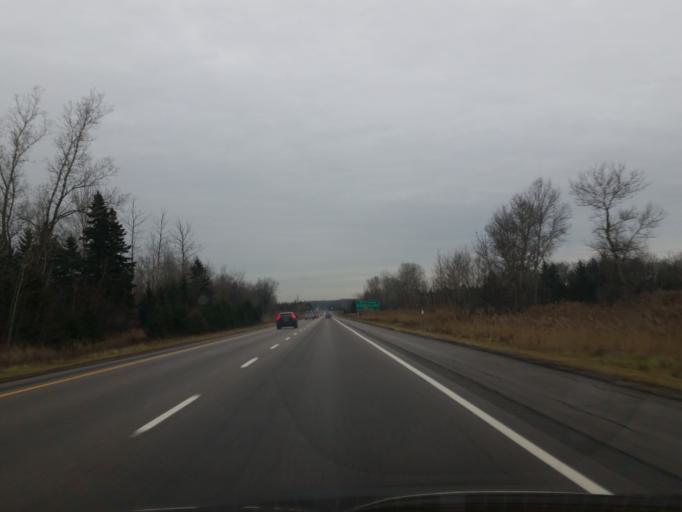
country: CA
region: Quebec
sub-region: Capitale-Nationale
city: Saint-Augustin-de-Desmaures
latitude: 46.7491
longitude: -71.5079
